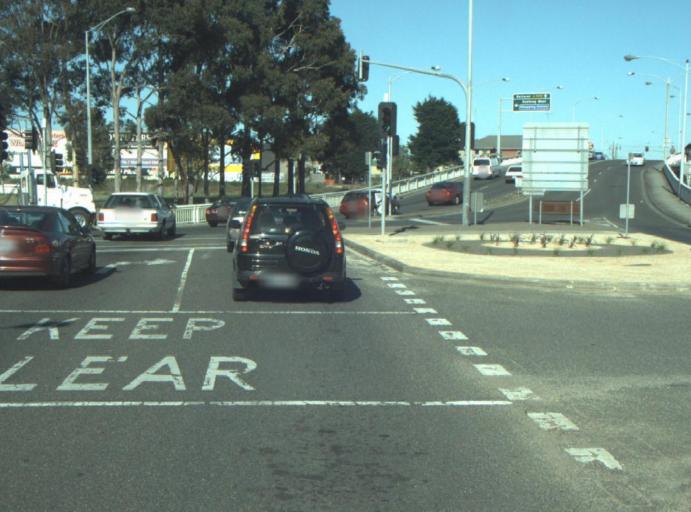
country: AU
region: Victoria
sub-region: Greater Geelong
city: Geelong West
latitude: -38.1325
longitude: 144.3525
